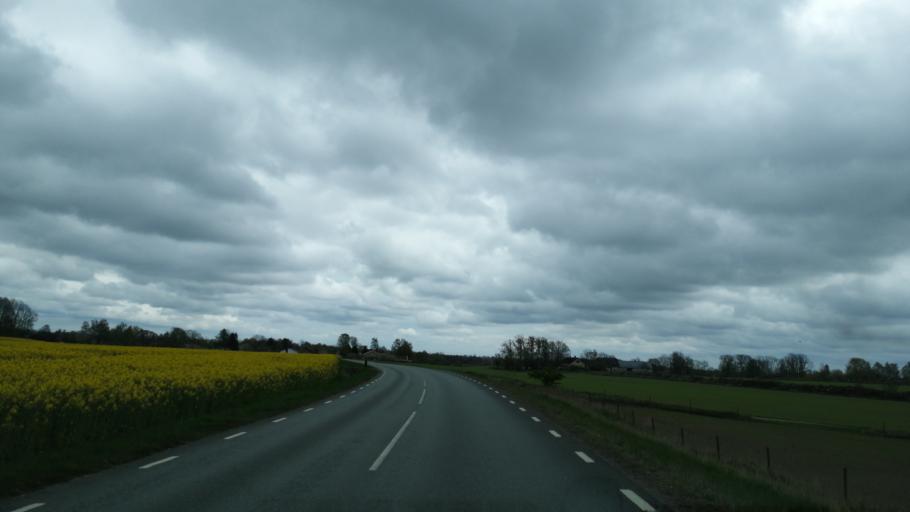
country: SE
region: Skane
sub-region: Kristianstads Kommun
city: Onnestad
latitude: 55.9932
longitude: 14.0245
